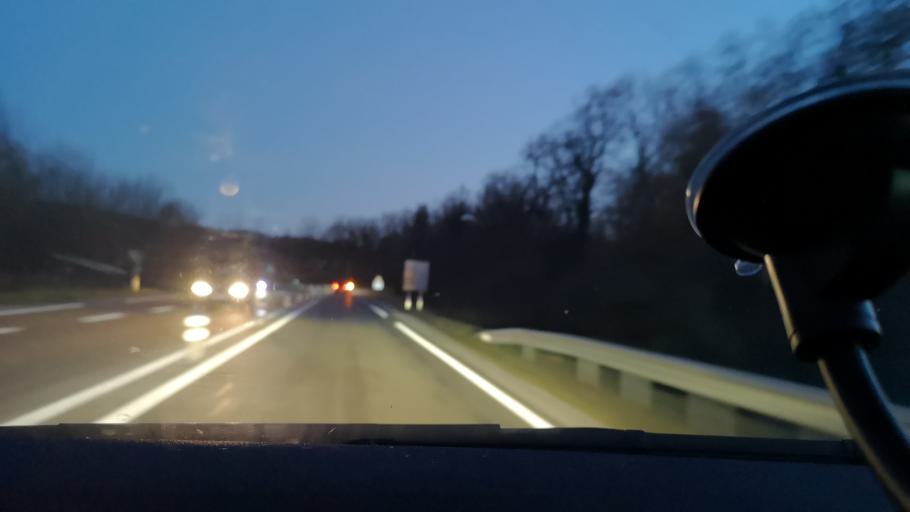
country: FR
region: Franche-Comte
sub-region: Departement du Jura
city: Champagnole
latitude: 46.7461
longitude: 5.9230
